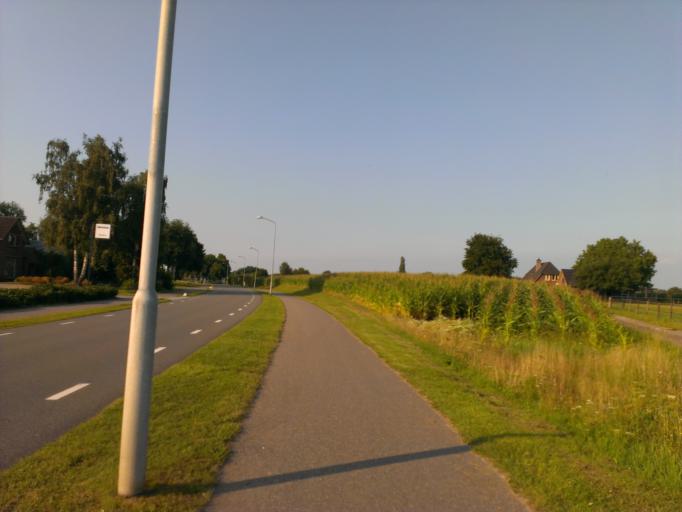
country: NL
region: Gelderland
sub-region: Gemeente Heerde
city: Heerde
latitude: 52.3984
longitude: 6.0497
